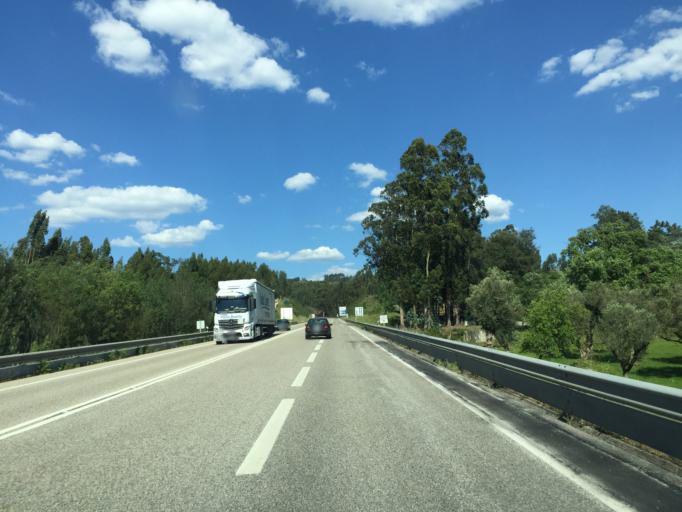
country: PT
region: Leiria
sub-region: Figueiro Dos Vinhos
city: Figueiro dos Vinhos
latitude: 39.9160
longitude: -8.3525
